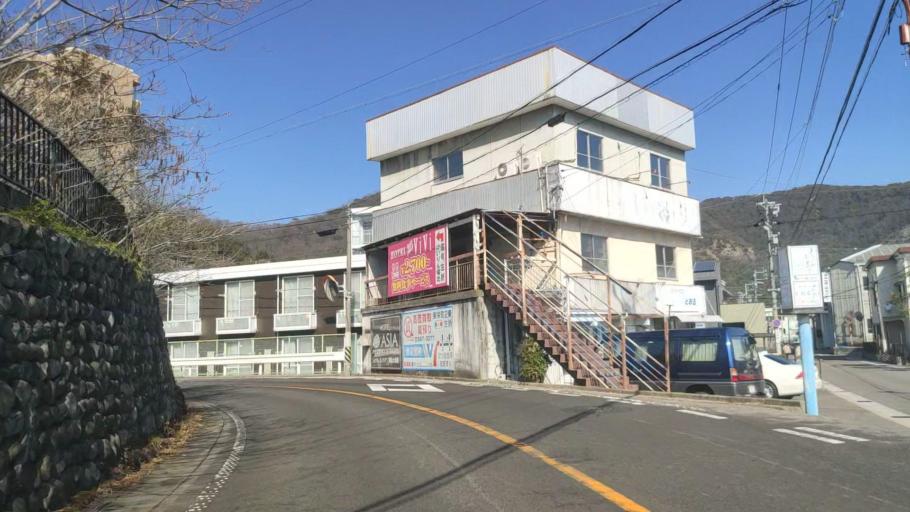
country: JP
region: Gifu
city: Gifu-shi
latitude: 35.4181
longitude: 136.7758
